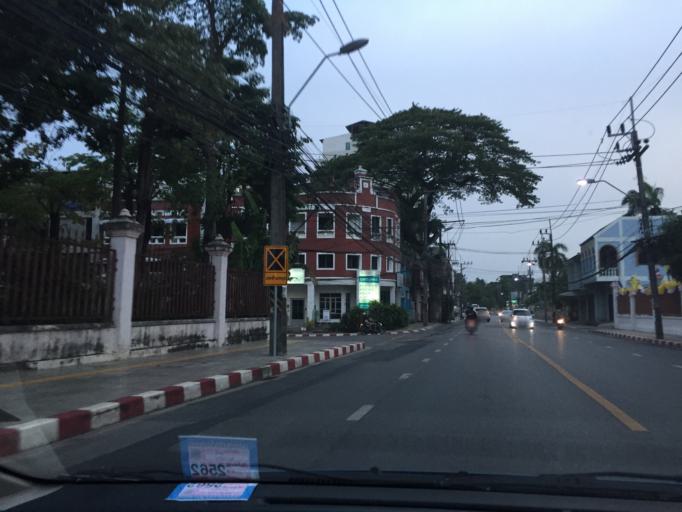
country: TH
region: Phuket
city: Wichit
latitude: 7.8920
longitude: 98.3859
